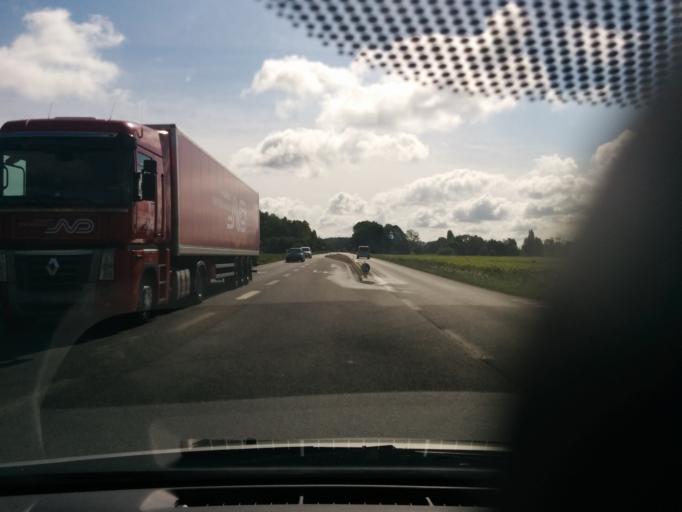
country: FR
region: Pays de la Loire
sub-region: Departement de Maine-et-Loire
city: Baune
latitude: 47.4741
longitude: -0.3197
